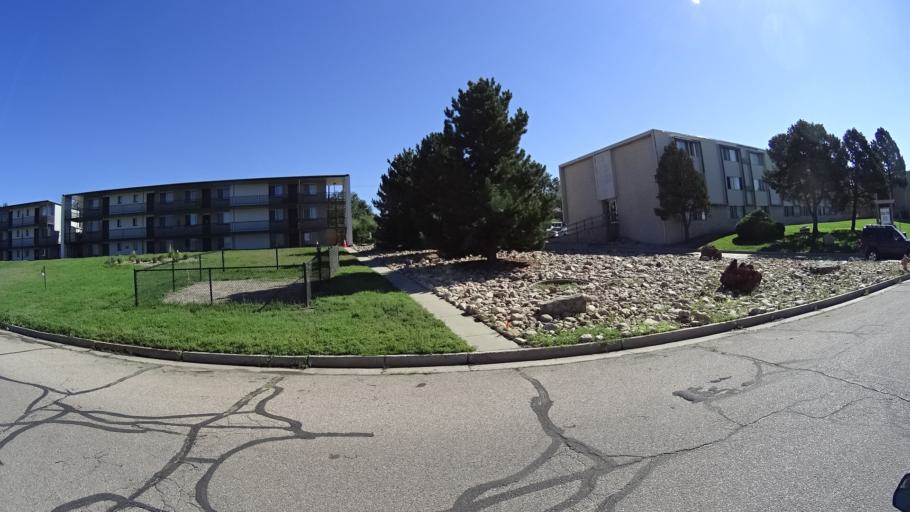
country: US
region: Colorado
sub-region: El Paso County
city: Colorado Springs
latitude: 38.8603
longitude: -104.7929
